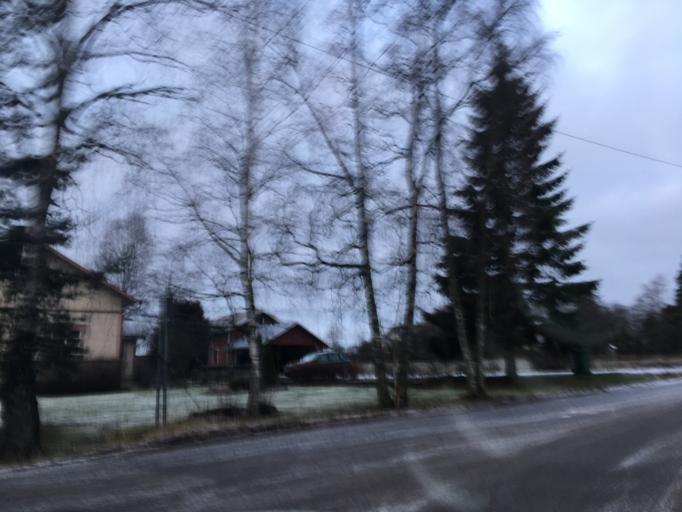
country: FI
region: Varsinais-Suomi
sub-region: Loimaa
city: Aura
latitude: 60.6084
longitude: 22.5627
